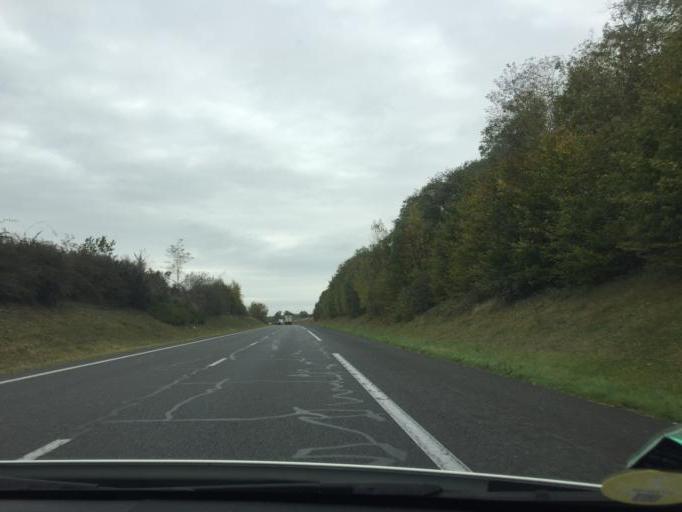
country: FR
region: Bourgogne
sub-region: Departement de l'Yonne
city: Egriselles-le-Bocage
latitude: 48.0783
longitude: 3.1251
